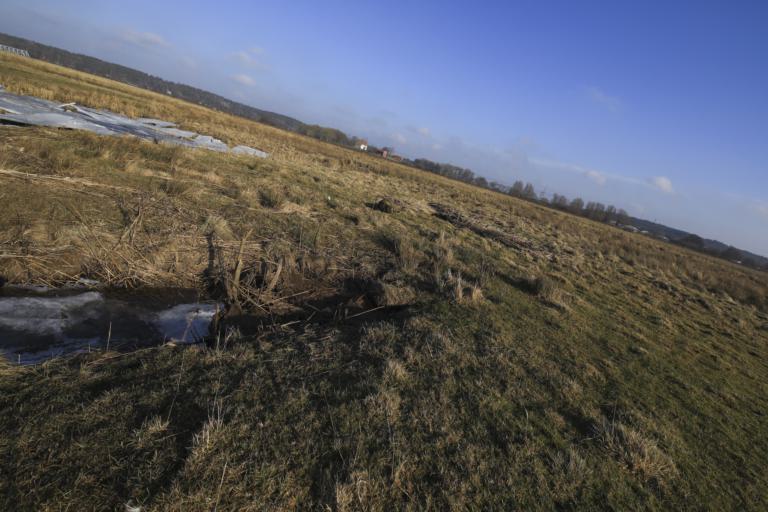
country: SE
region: Halland
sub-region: Kungsbacka Kommun
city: Frillesas
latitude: 57.2218
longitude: 12.2132
